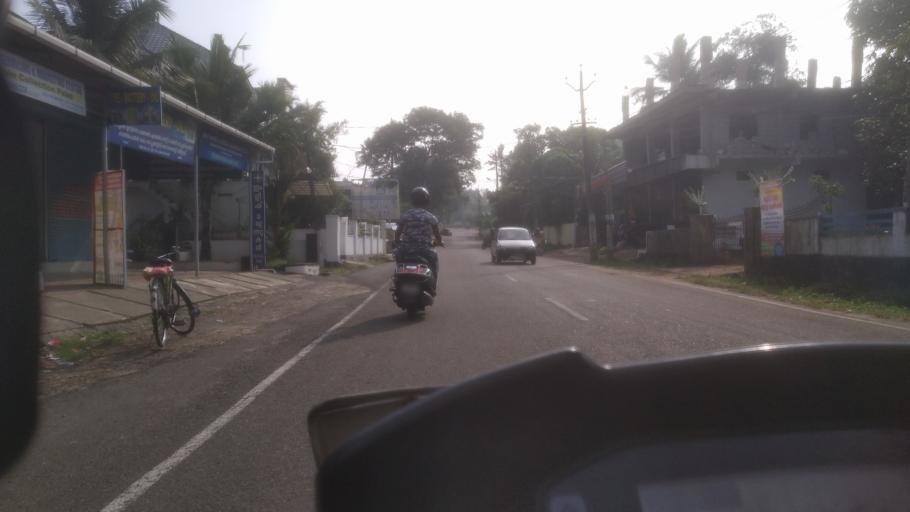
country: IN
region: Kerala
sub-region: Ernakulam
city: Angamali
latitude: 10.1623
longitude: 76.3708
